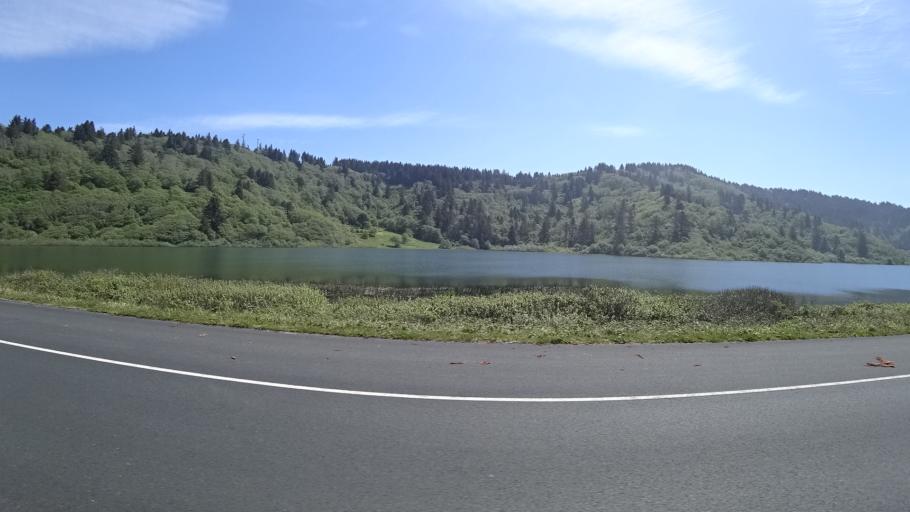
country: US
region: California
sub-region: Humboldt County
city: Westhaven-Moonstone
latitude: 41.2754
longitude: -124.0947
